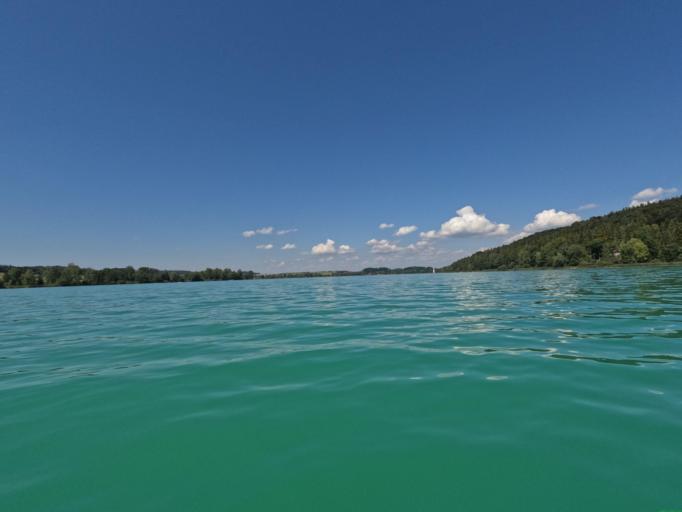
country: DE
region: Bavaria
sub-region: Upper Bavaria
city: Taching am See
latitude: 47.9712
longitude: 12.7452
